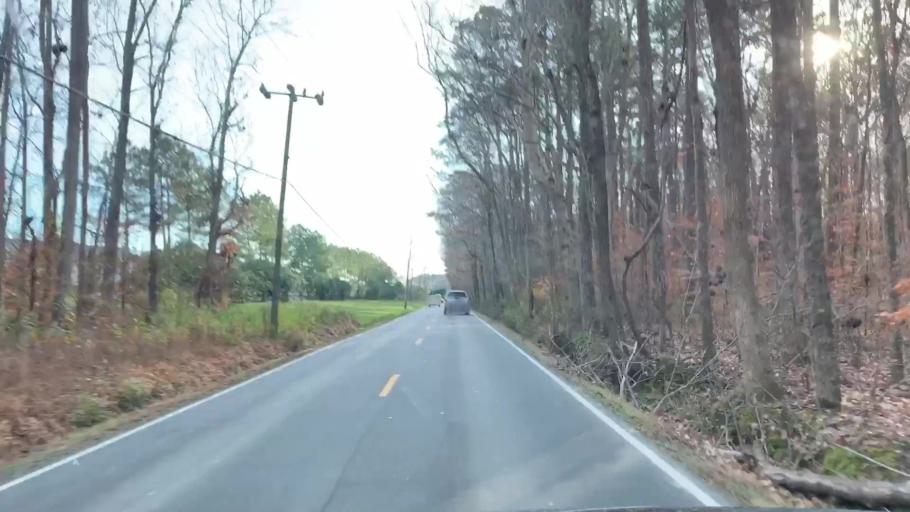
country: US
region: Virginia
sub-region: City of Virginia Beach
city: Virginia Beach
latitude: 36.7254
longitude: -76.0722
